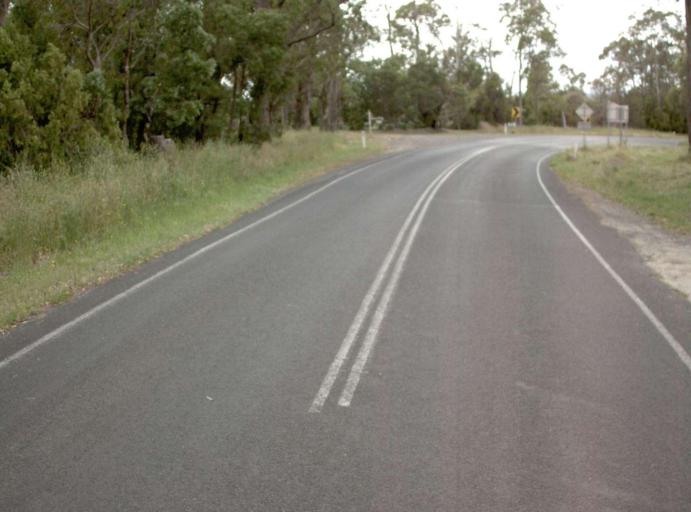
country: AU
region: Victoria
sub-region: Latrobe
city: Moe
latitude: -38.1256
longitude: 146.2545
